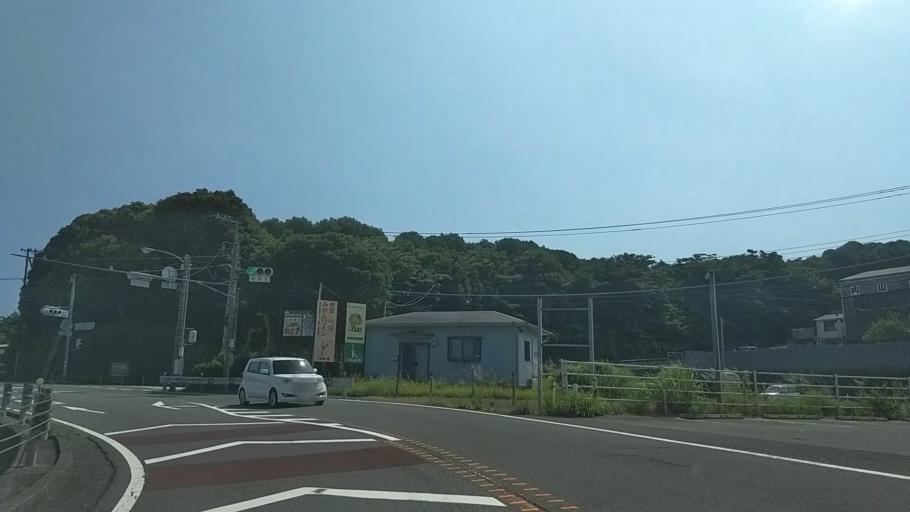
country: JP
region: Shizuoka
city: Shimoda
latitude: 34.7832
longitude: 139.0511
